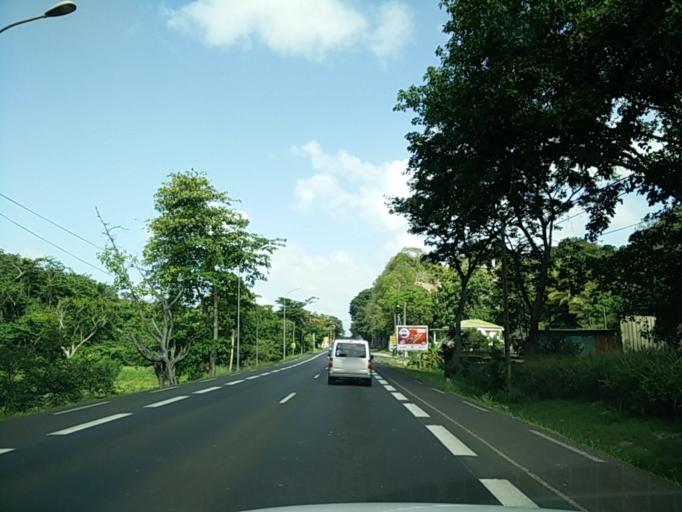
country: GP
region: Guadeloupe
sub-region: Guadeloupe
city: Le Gosier
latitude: 16.2179
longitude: -61.4900
